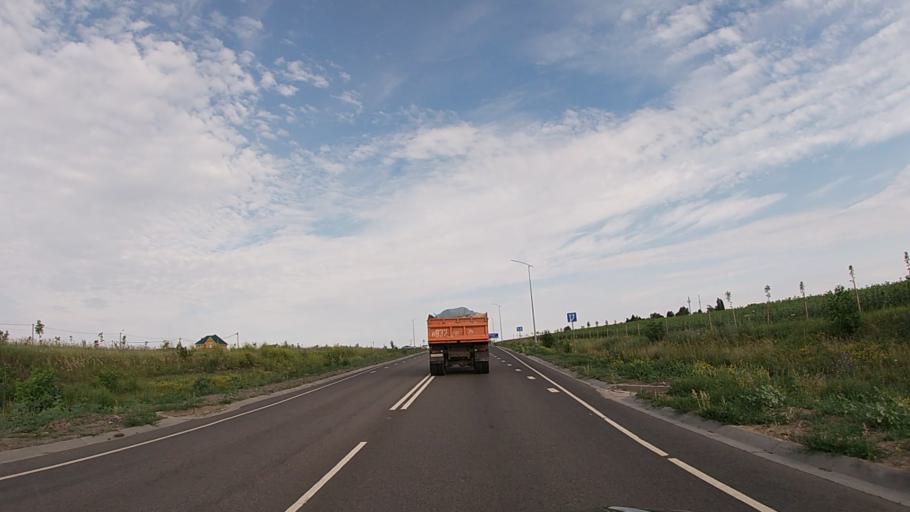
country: RU
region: Belgorod
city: Severnyy
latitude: 50.6711
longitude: 36.4831
